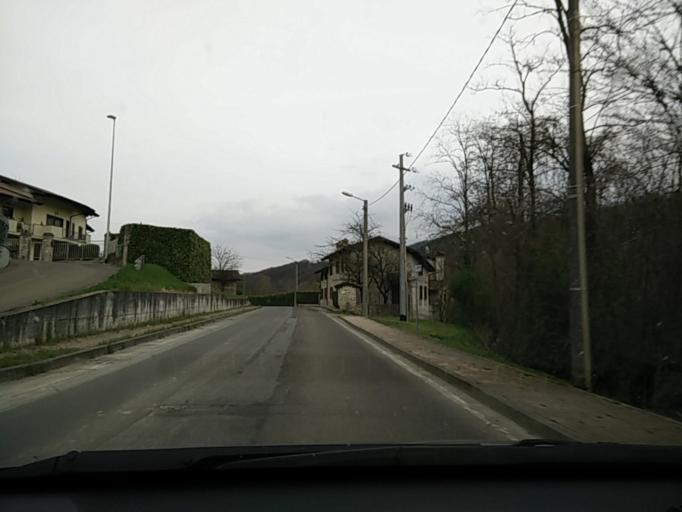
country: IT
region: Lombardy
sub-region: Provincia di Pavia
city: Godiasco
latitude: 44.8943
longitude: 9.0634
